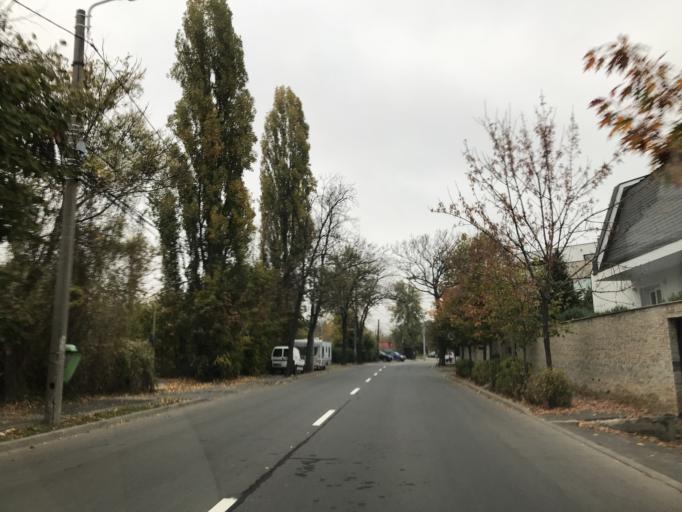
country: RO
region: Bucuresti
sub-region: Municipiul Bucuresti
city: Bucuresti
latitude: 44.4821
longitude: 26.0668
